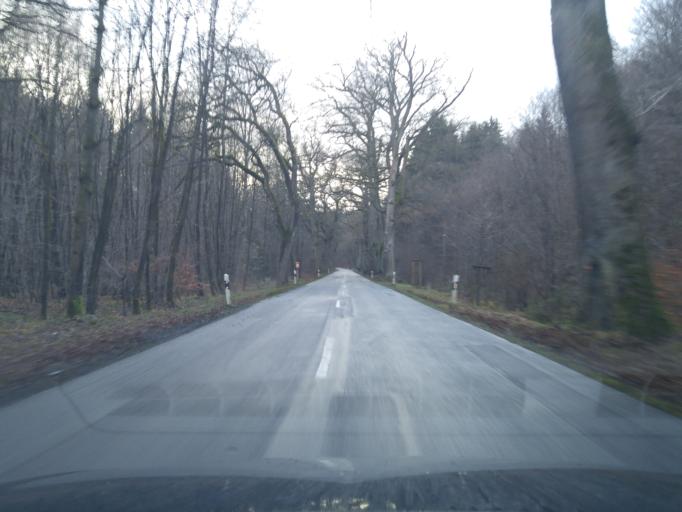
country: DE
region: Hesse
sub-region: Regierungsbezirk Kassel
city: Udenhausen
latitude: 51.4920
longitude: 9.5626
